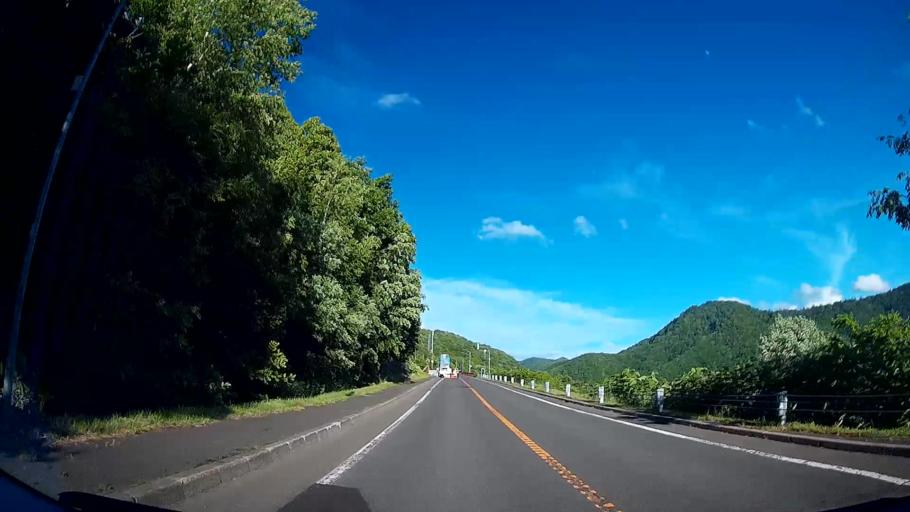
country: JP
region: Hokkaido
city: Sapporo
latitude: 42.9778
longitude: 141.1404
